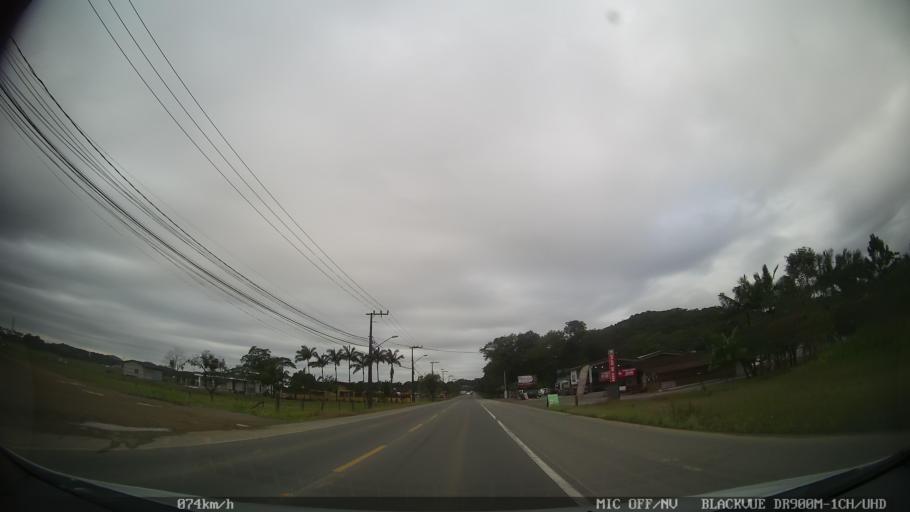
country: BR
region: Santa Catarina
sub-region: Joinville
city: Joinville
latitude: -26.2734
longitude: -48.9239
